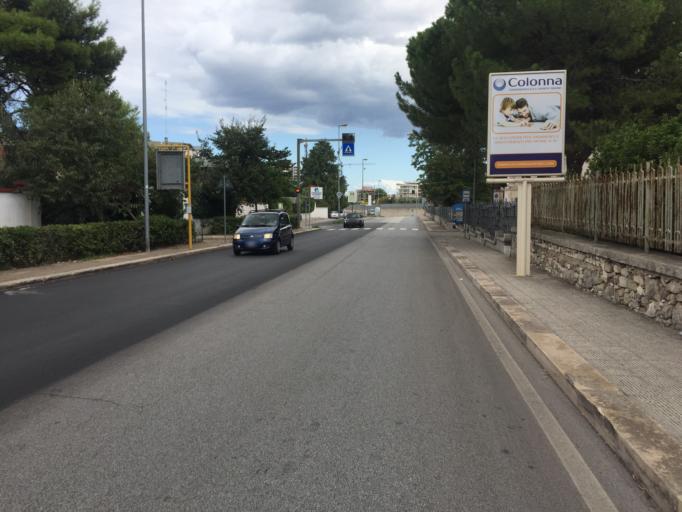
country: IT
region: Apulia
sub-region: Provincia di Bari
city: Bari
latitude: 41.1010
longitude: 16.8474
